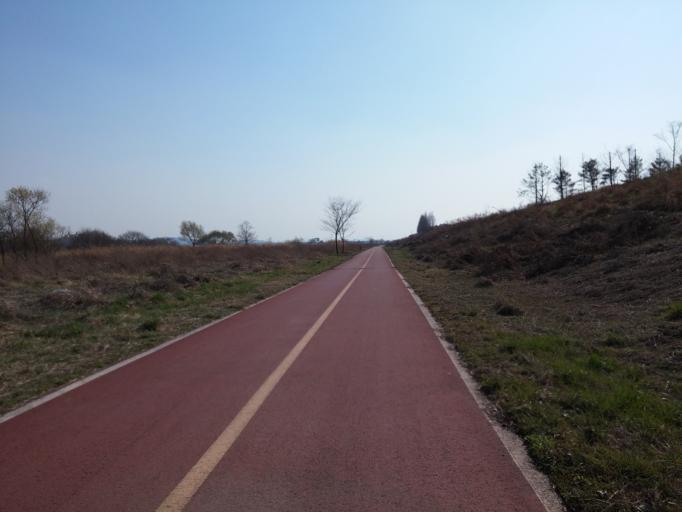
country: KR
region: Chungcheongbuk-do
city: Cheongju-si
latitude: 36.6341
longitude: 127.3547
